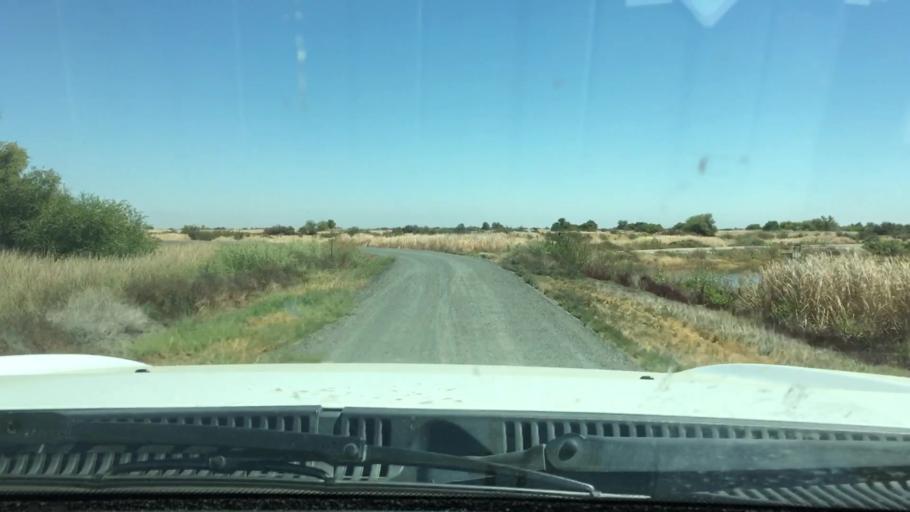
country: US
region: California
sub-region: Kern County
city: Lost Hills
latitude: 35.7480
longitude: -119.5952
